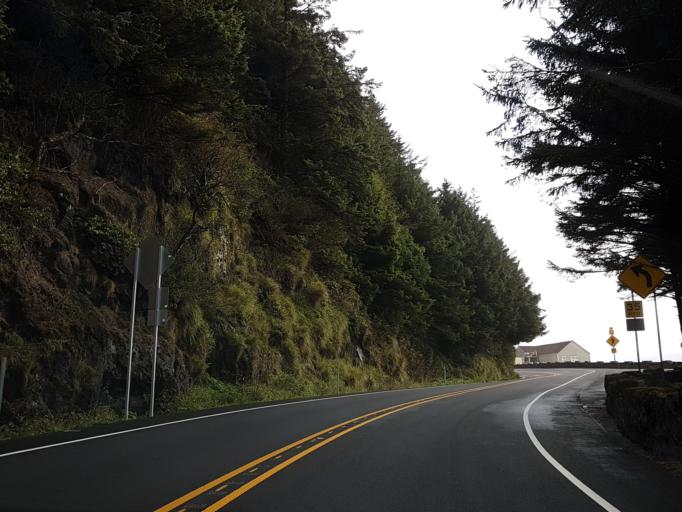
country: US
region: Oregon
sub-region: Lane County
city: Florence
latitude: 44.1235
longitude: -124.1262
